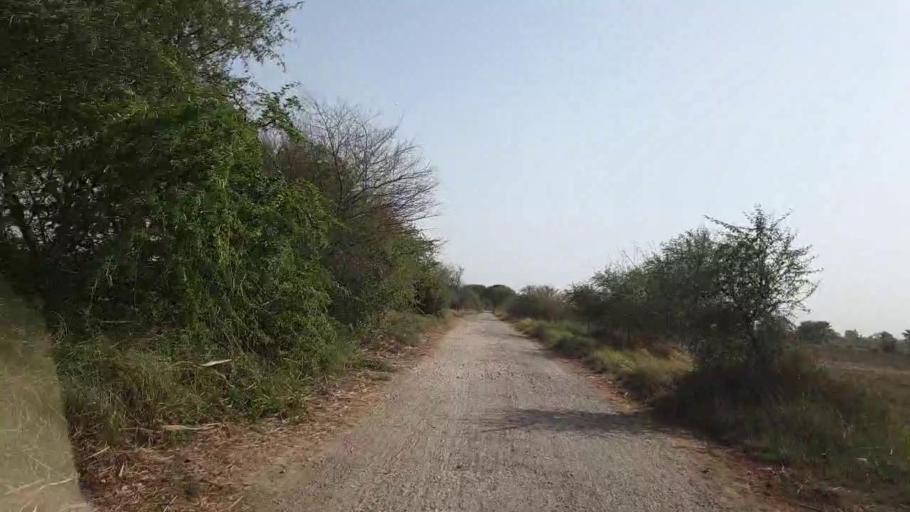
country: PK
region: Sindh
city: Tando Ghulam Ali
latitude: 25.0819
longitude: 68.8369
